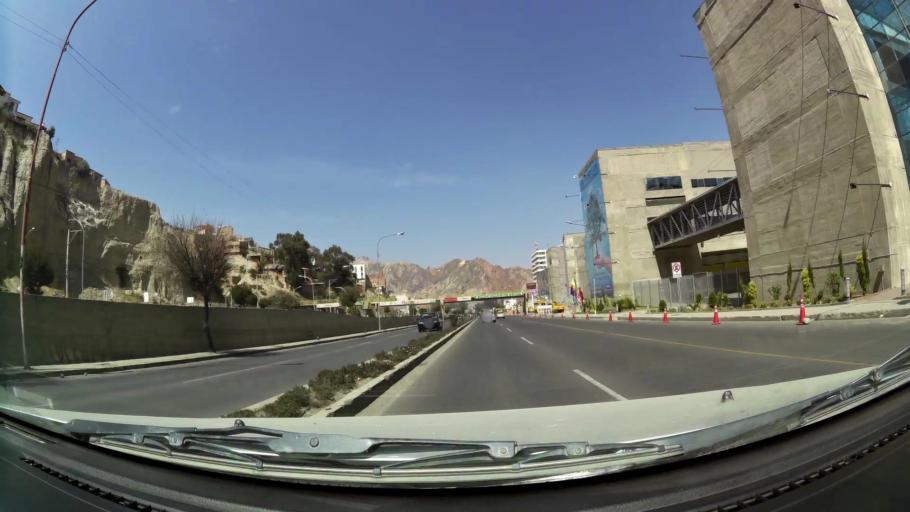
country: BO
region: La Paz
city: La Paz
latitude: -16.5360
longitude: -68.0963
